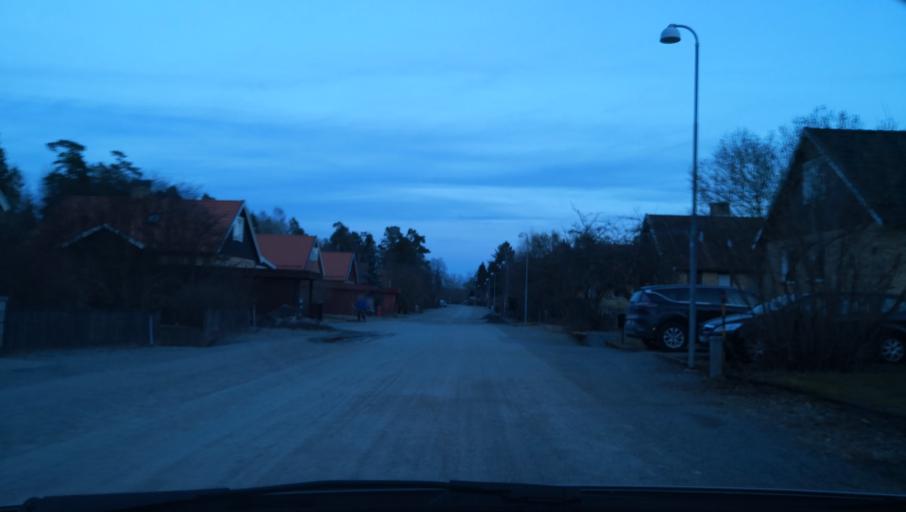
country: SE
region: Stockholm
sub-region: Varmdo Kommun
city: Gustavsberg
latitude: 59.3387
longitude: 18.3867
